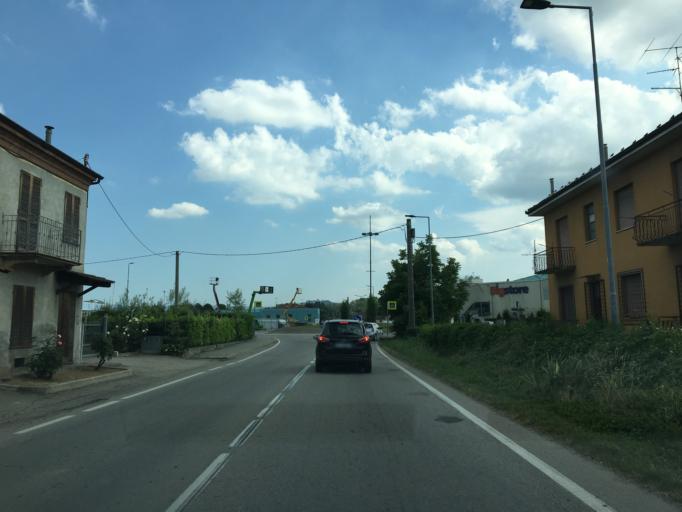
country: IT
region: Piedmont
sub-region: Provincia di Cuneo
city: Mussotto
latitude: 44.7220
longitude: 8.0094
